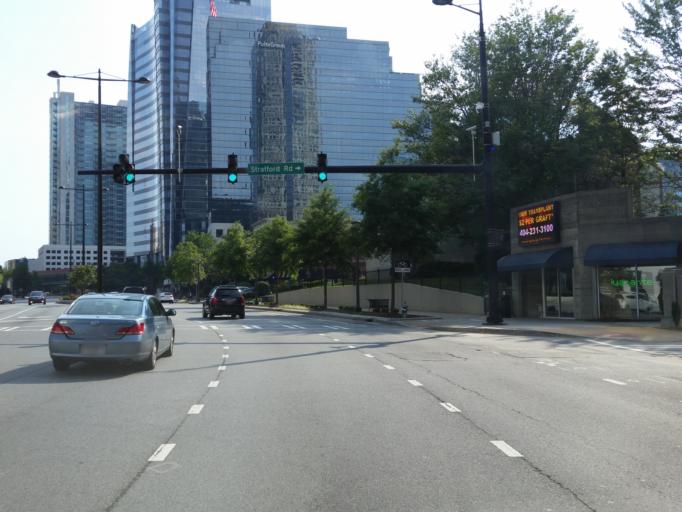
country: US
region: Georgia
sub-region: DeKalb County
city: North Atlanta
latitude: 33.8486
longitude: -84.3665
